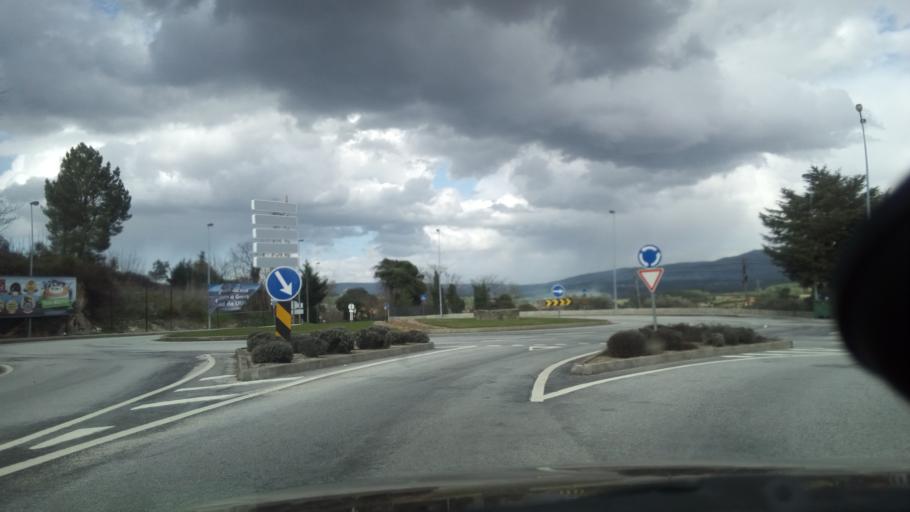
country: PT
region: Guarda
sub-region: Celorico da Beira
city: Celorico da Beira
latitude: 40.6451
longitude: -7.3851
